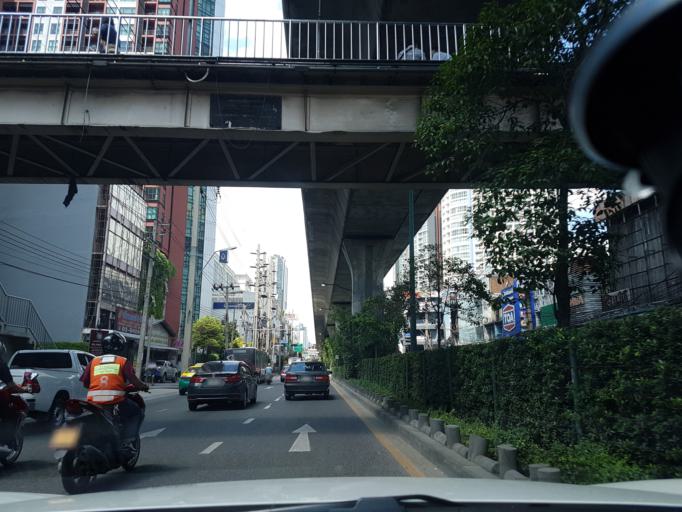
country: TH
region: Bangkok
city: Phra Khanong
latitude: 13.7125
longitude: 100.5949
